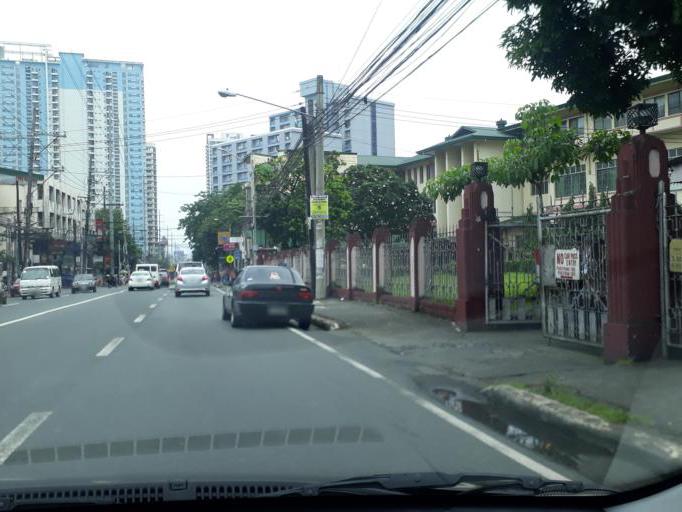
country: PH
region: Calabarzon
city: Del Monte
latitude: 14.6223
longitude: 121.0257
